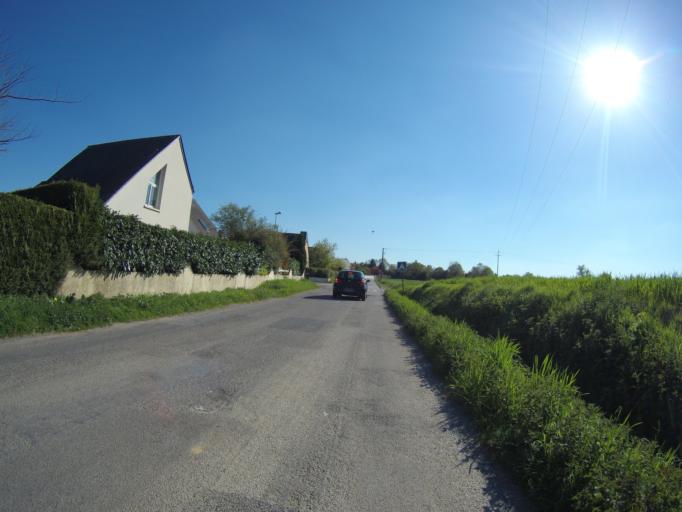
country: FR
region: Brittany
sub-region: Departement d'Ille-et-Vilaine
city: Vern-sur-Seiche
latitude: 48.0467
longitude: -1.6202
